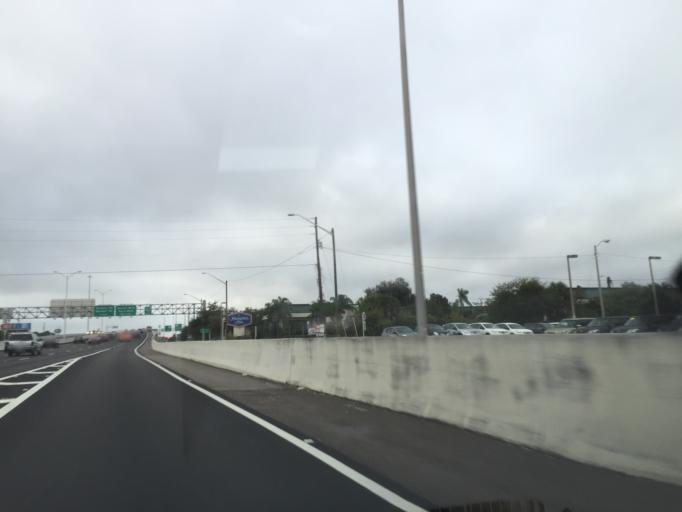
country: US
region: Florida
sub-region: Pinellas County
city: Safety Harbor
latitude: 27.9648
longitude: -82.7301
